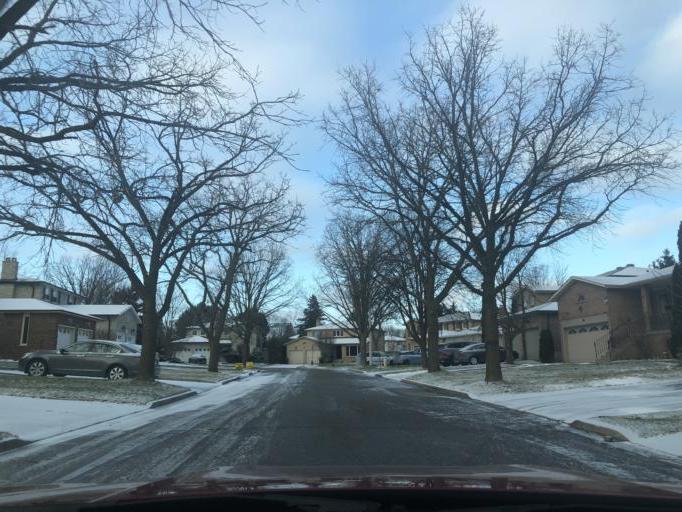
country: CA
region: Ontario
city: Markham
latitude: 43.8736
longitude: -79.2386
